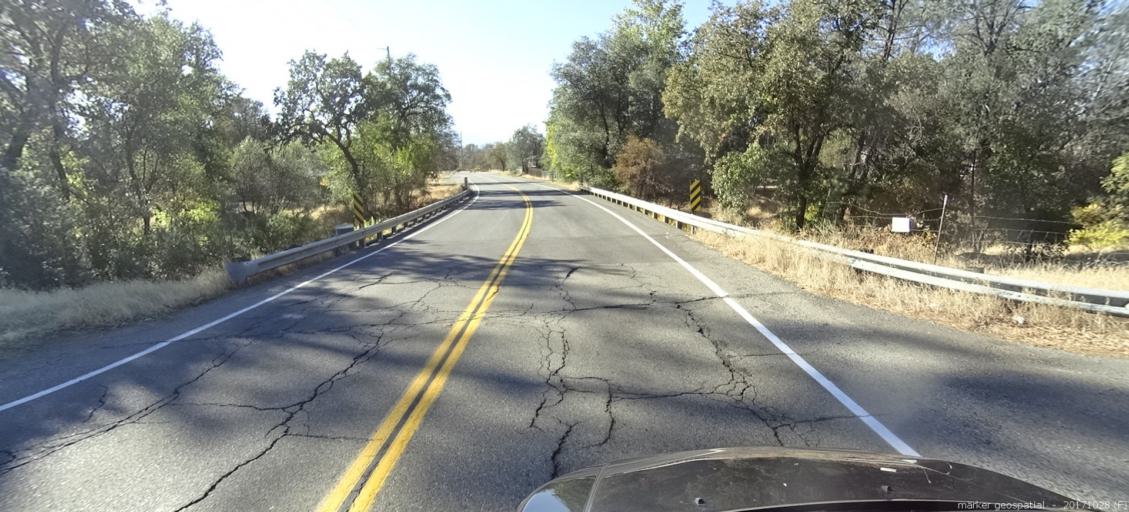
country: US
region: California
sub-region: Shasta County
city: Shasta Lake
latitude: 40.6423
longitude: -122.3690
